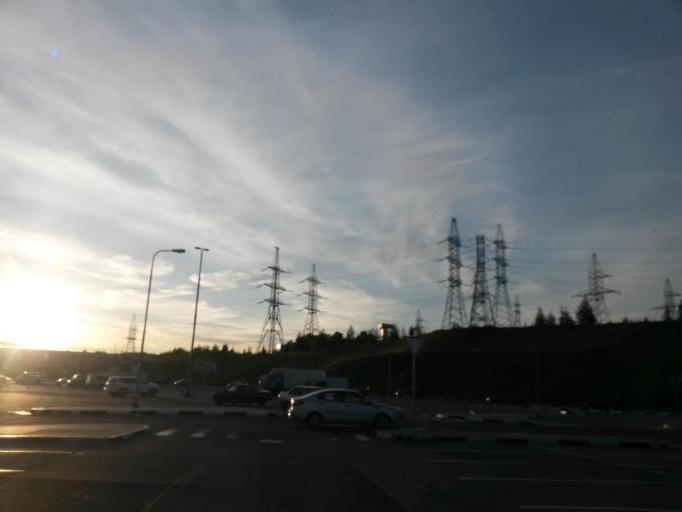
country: RU
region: Moscow
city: Tyoply Stan
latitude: 55.6066
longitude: 37.4937
